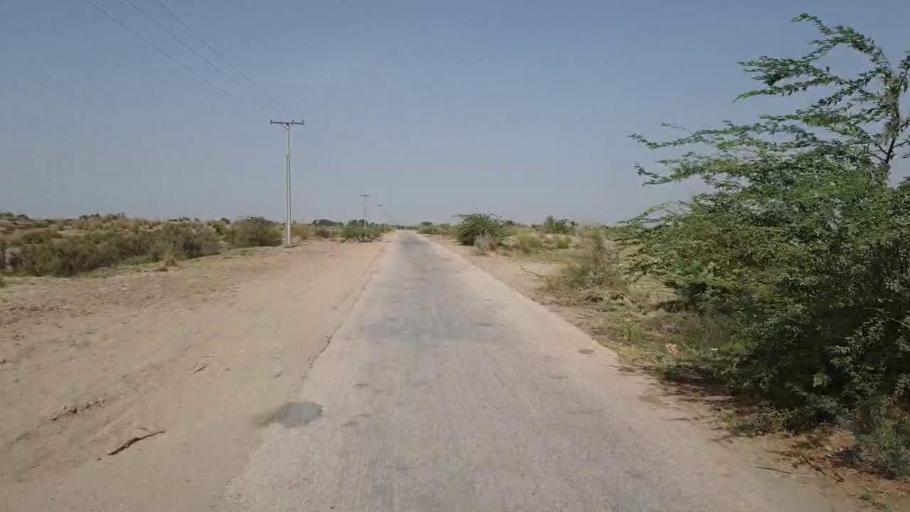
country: PK
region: Sindh
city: Jam Sahib
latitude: 26.4086
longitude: 68.8965
